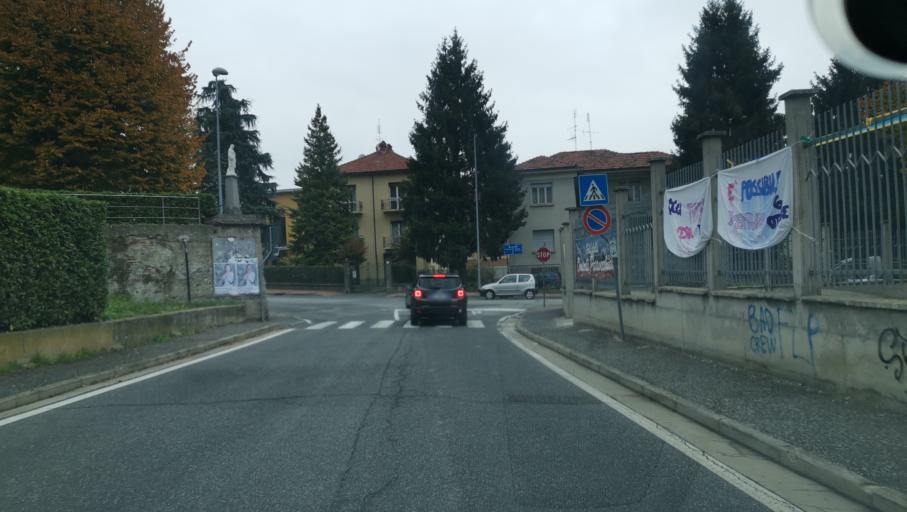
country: IT
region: Piedmont
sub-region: Provincia di Torino
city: Gassino Torinese
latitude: 45.1289
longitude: 7.8265
